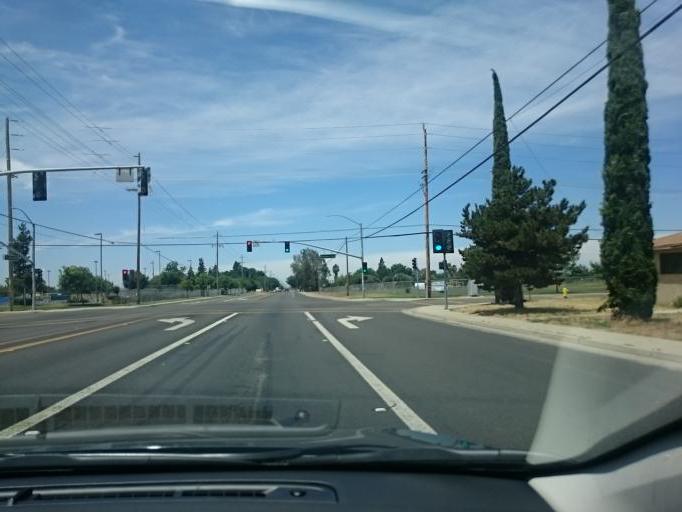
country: US
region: California
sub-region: Stanislaus County
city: Waterford
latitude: 37.6382
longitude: -120.7733
